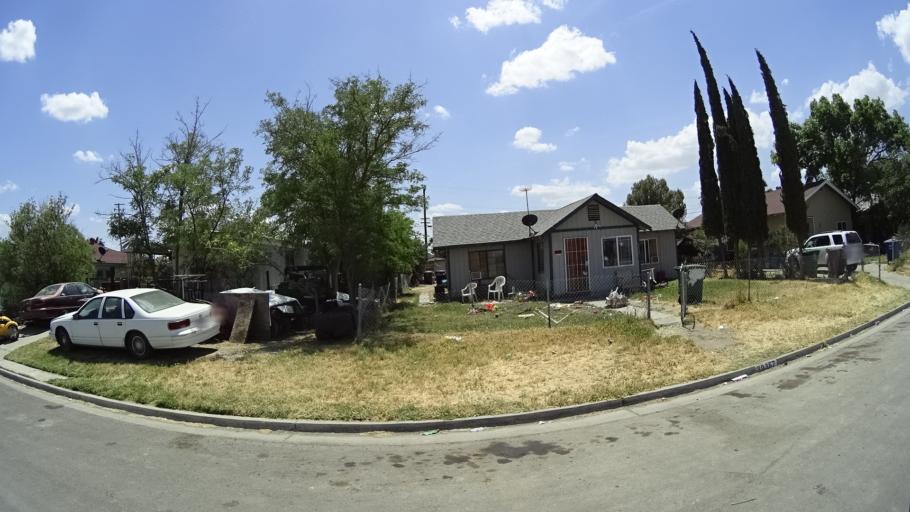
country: US
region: California
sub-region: Kings County
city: Stratford
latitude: 36.1917
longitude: -119.8232
